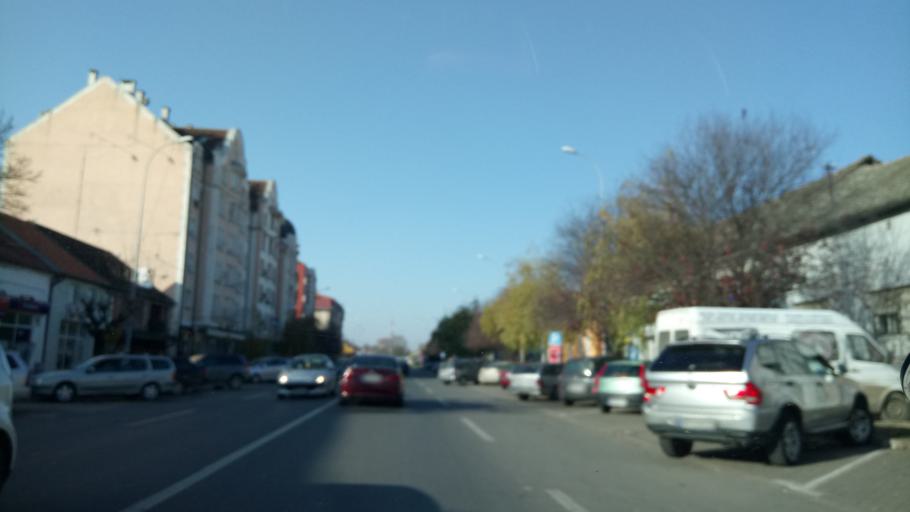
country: RS
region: Autonomna Pokrajina Vojvodina
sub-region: Sremski Okrug
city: Ingija
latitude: 45.0486
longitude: 20.0798
